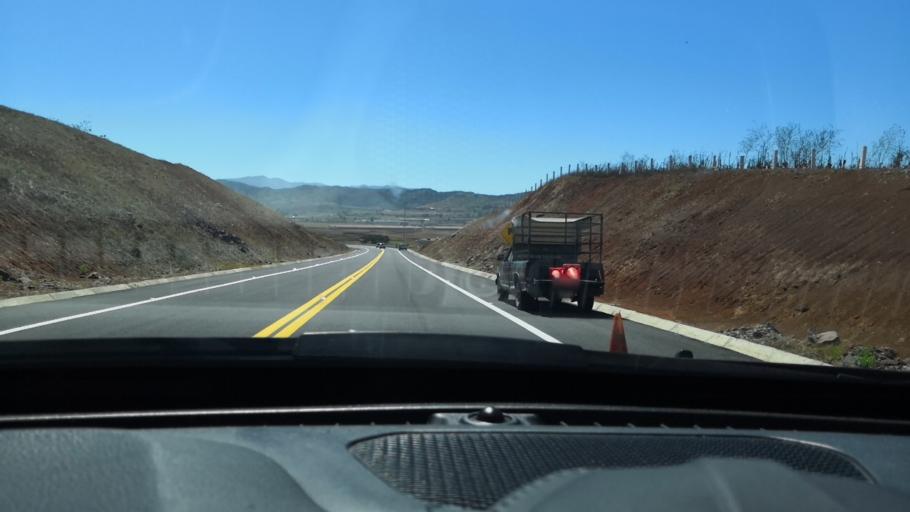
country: MX
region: Nayarit
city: Compostela
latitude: 21.2152
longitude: -104.8830
